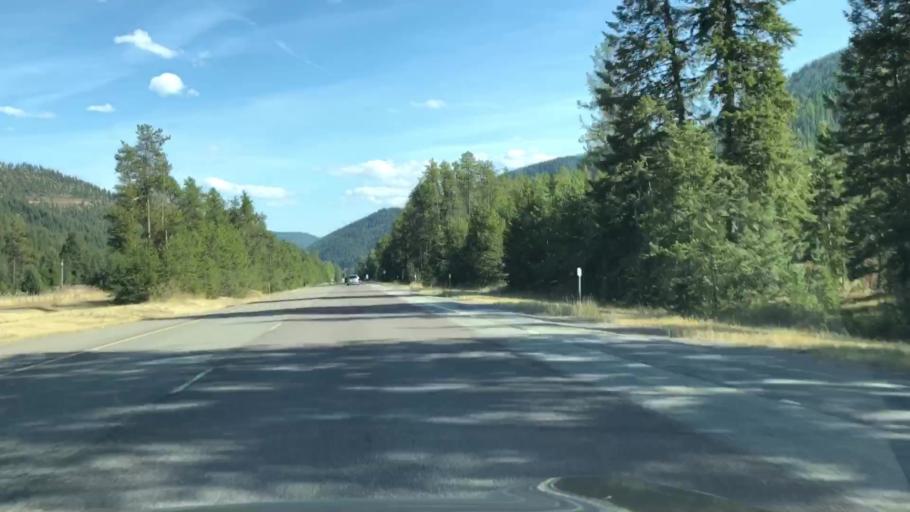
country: US
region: Montana
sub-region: Sanders County
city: Thompson Falls
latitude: 47.3730
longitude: -115.3442
